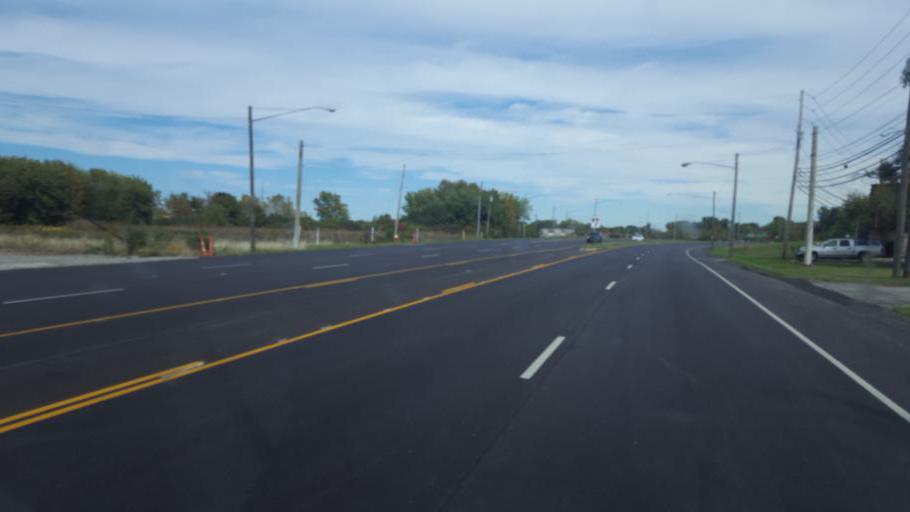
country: US
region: Ohio
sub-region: Lorain County
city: Amherst
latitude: 41.4442
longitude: -82.2293
